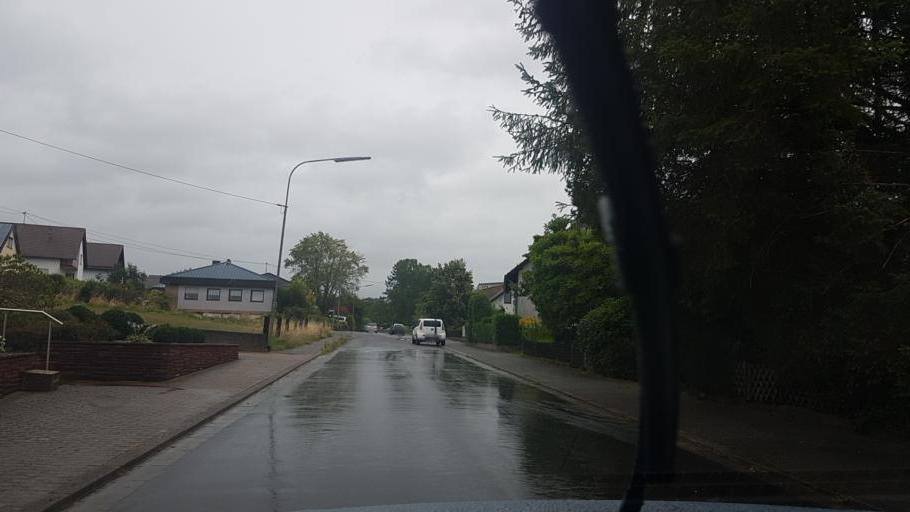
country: DE
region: Saarland
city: Losheim
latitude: 49.5135
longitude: 6.7500
